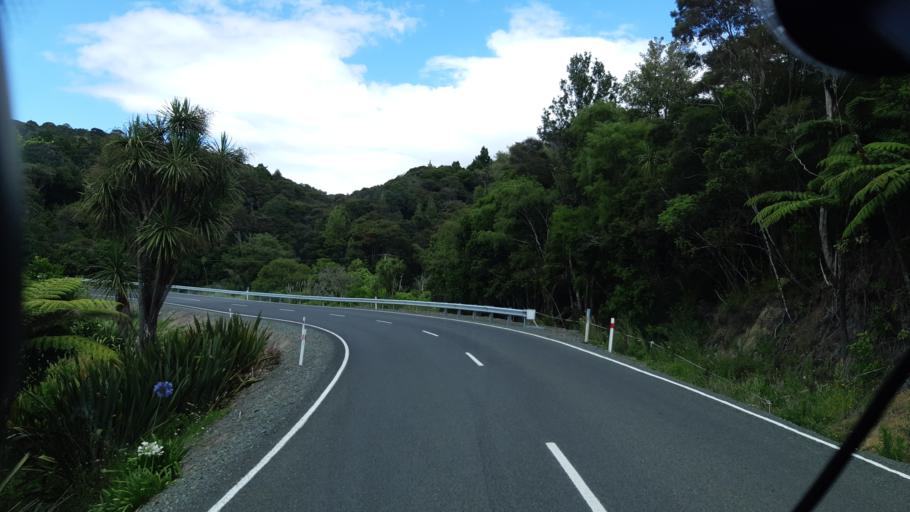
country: NZ
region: Northland
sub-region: Far North District
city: Taipa
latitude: -35.2427
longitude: 173.5354
